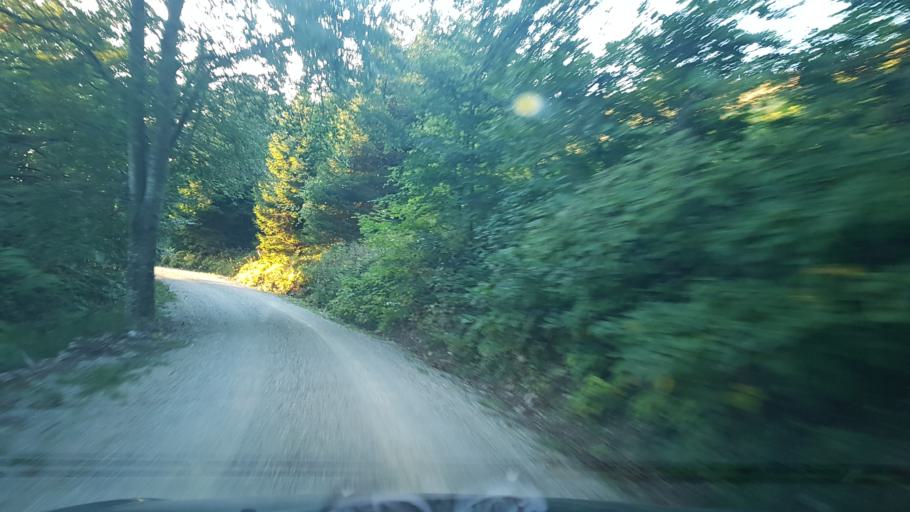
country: SI
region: Vipava
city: Vipava
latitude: 45.7839
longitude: 14.0389
